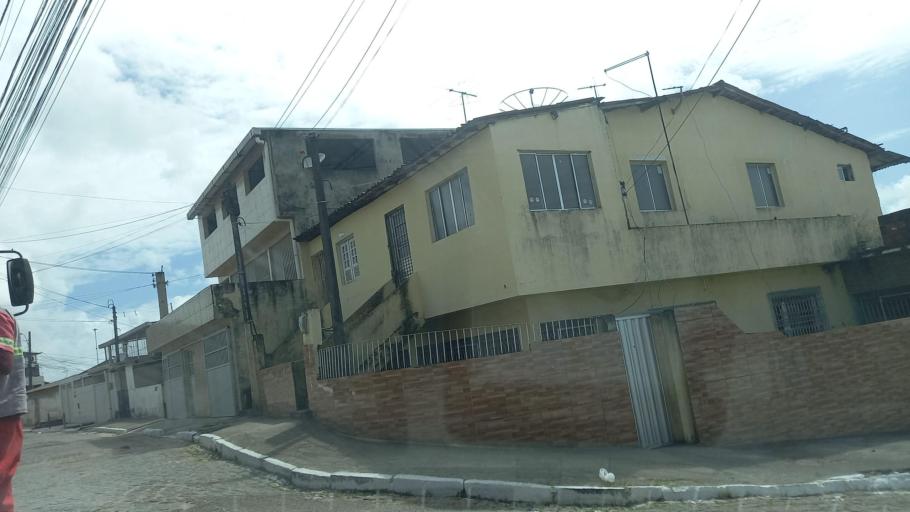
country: BR
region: Pernambuco
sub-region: Jaboatao Dos Guararapes
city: Jaboatao dos Guararapes
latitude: -8.1341
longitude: -34.9551
